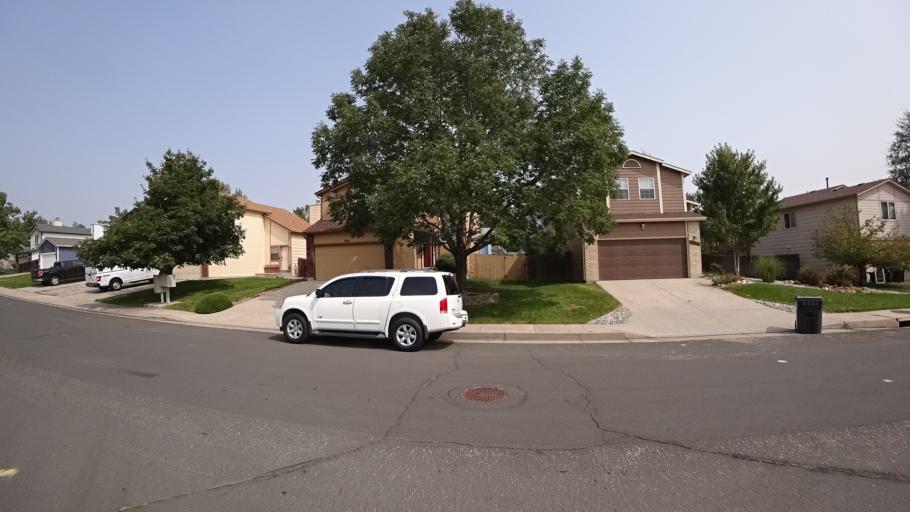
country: US
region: Colorado
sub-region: El Paso County
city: Cimarron Hills
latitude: 38.9200
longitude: -104.7261
